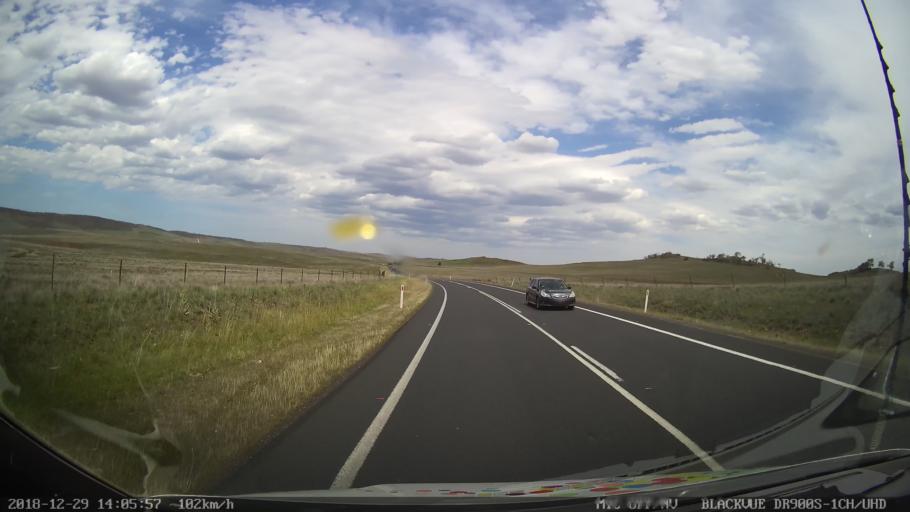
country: AU
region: New South Wales
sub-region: Cooma-Monaro
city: Cooma
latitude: -36.3377
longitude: 149.1954
